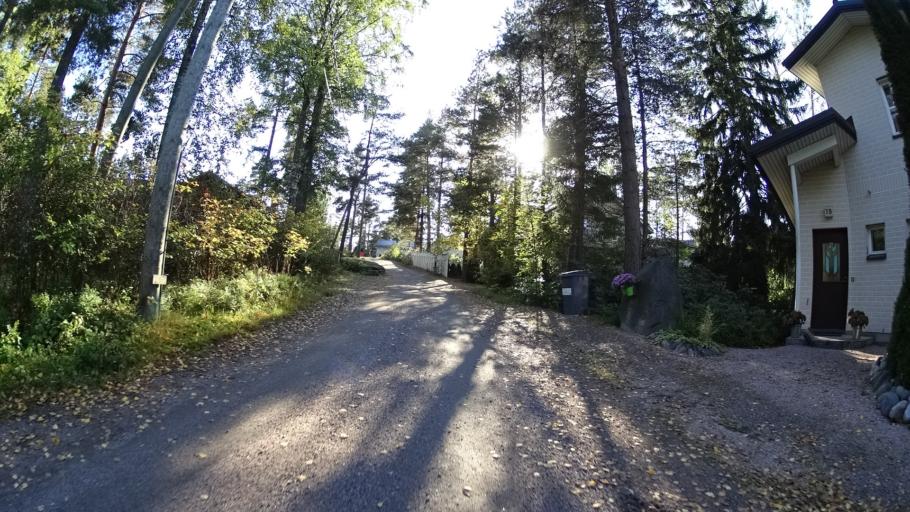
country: FI
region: Uusimaa
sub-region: Helsinki
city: Kilo
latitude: 60.2278
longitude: 24.7764
